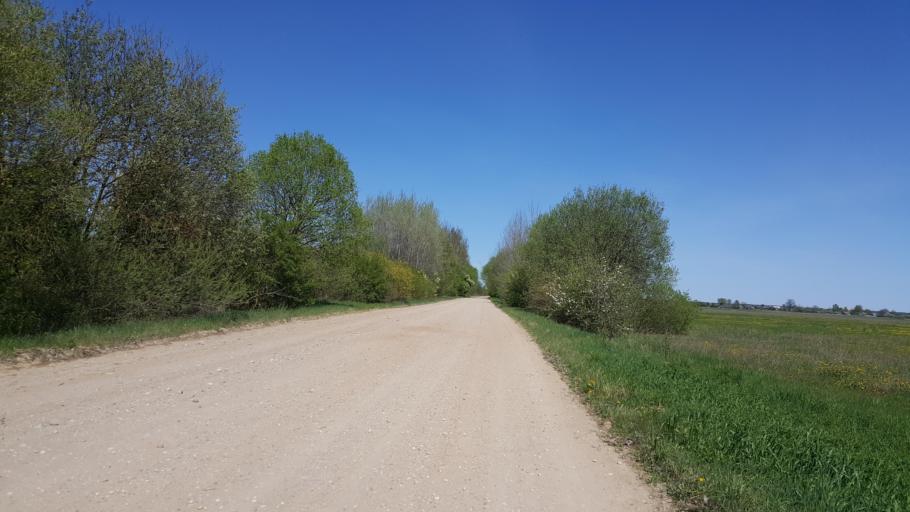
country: BY
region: Brest
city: Kamyanyets
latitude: 52.4498
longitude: 23.8675
